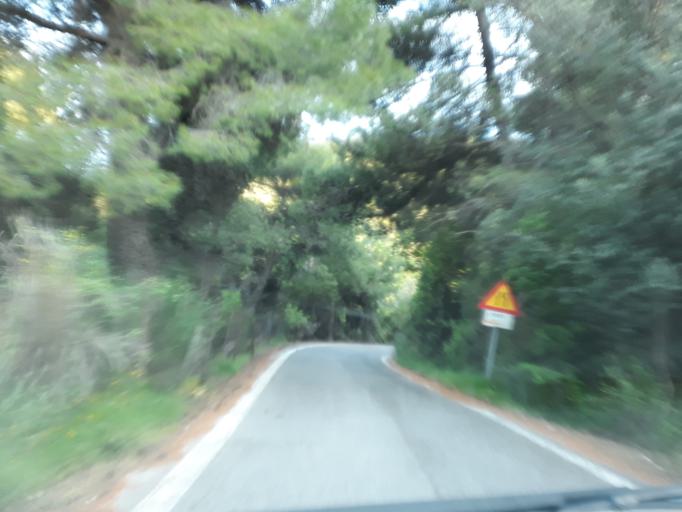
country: GR
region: Attica
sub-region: Nomarchia Anatolikis Attikis
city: Afidnes
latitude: 38.2284
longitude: 23.7882
